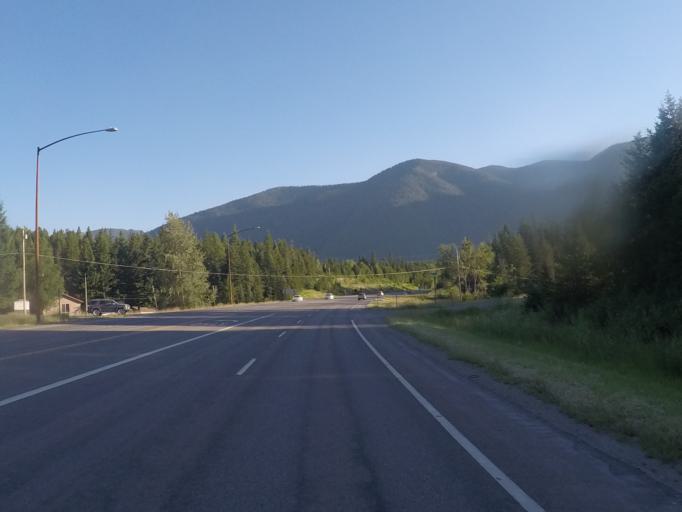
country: US
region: Montana
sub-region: Flathead County
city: Columbia Falls
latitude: 48.3914
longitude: -114.0416
